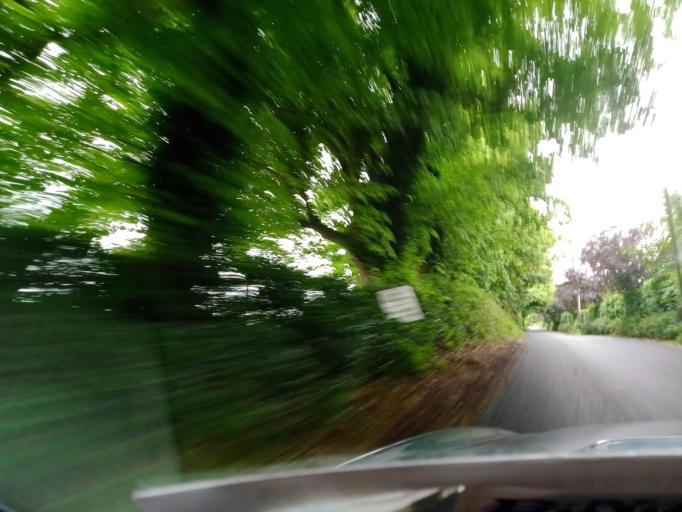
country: IE
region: Leinster
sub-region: Kilkenny
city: Thomastown
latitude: 52.5481
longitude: -7.2216
